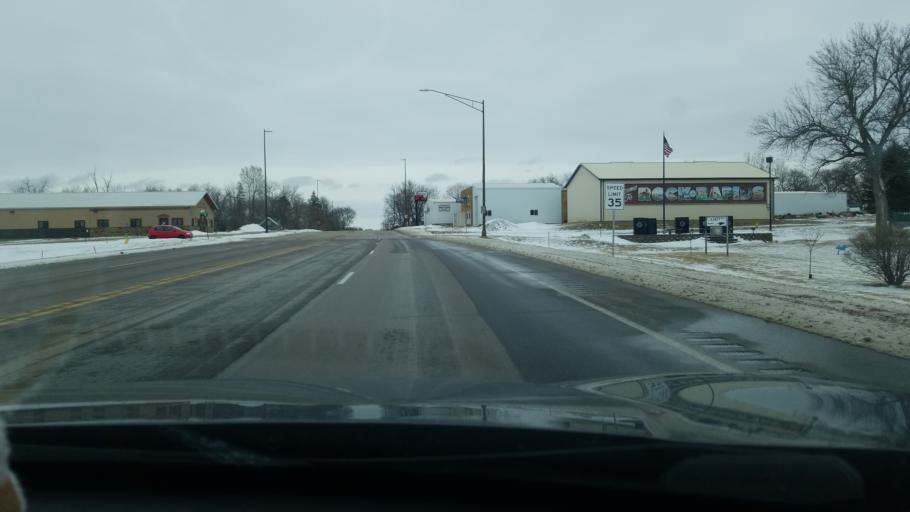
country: US
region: Iowa
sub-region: Lyon County
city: Rock Rapids
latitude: 43.4319
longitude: -96.1820
